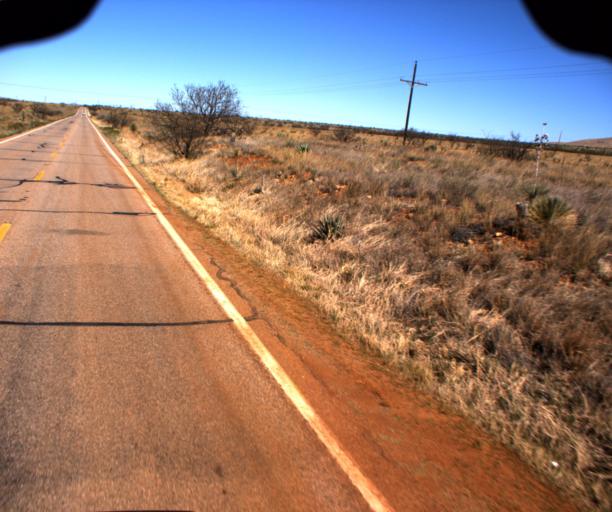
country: US
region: Arizona
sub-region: Cochise County
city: Huachuca City
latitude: 31.7129
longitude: -110.4579
